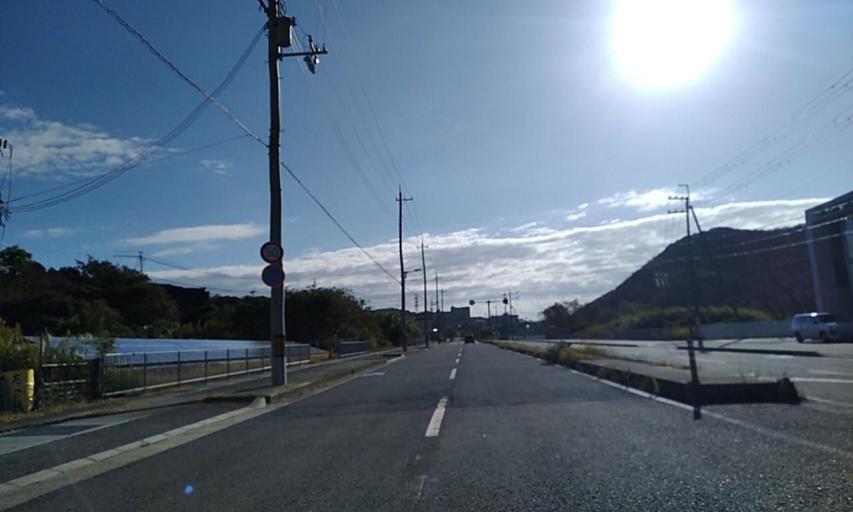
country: JP
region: Wakayama
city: Minato
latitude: 34.2694
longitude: 135.0875
